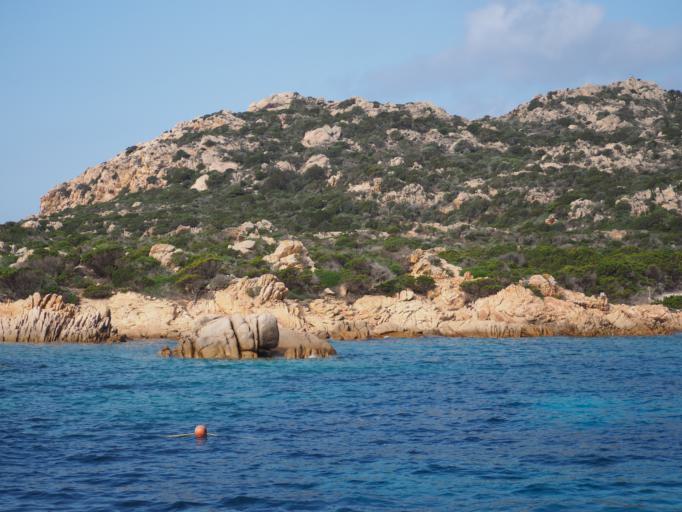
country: IT
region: Sardinia
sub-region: Provincia di Olbia-Tempio
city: La Maddalena
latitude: 41.2777
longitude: 9.3577
